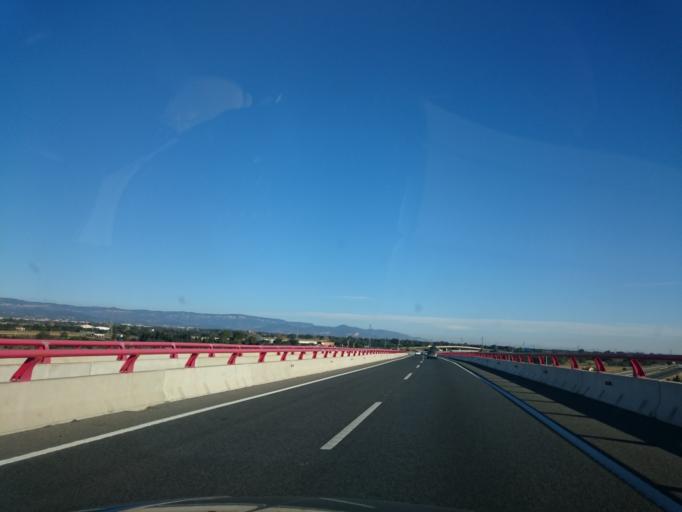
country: ES
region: Catalonia
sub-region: Provincia de Tarragona
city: Cambrils
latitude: 41.0707
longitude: 1.0128
